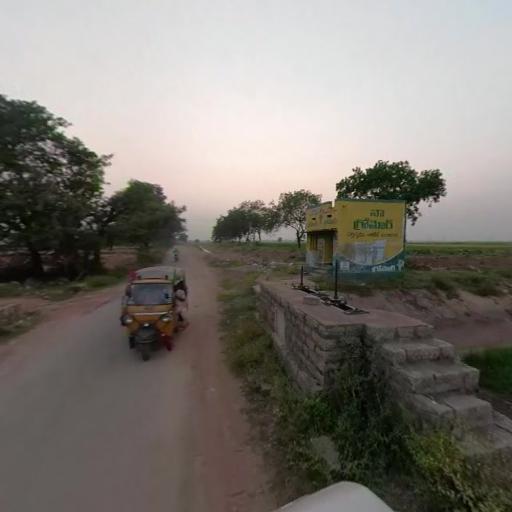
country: IN
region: Telangana
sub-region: Nalgonda
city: Suriapet
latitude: 17.1133
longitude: 79.5288
